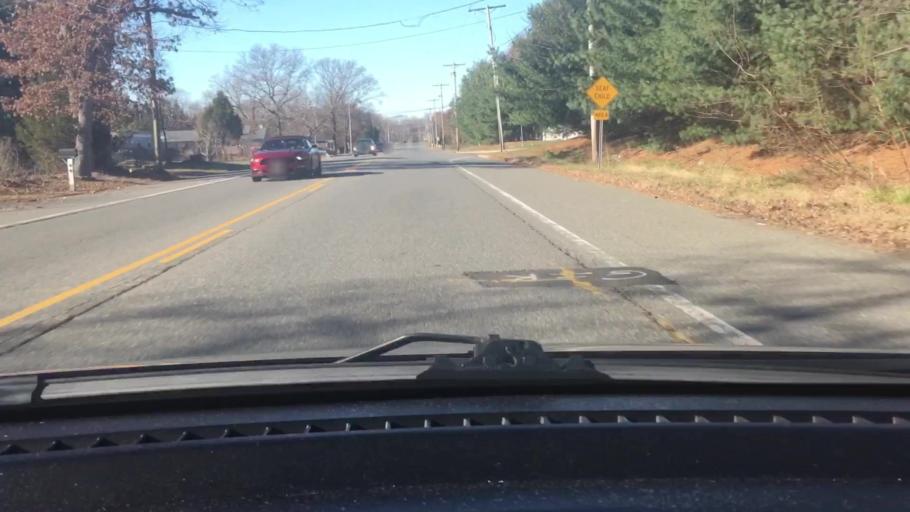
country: US
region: New Jersey
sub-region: Ocean County
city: Leisure Knoll
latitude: 40.0285
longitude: -74.2789
